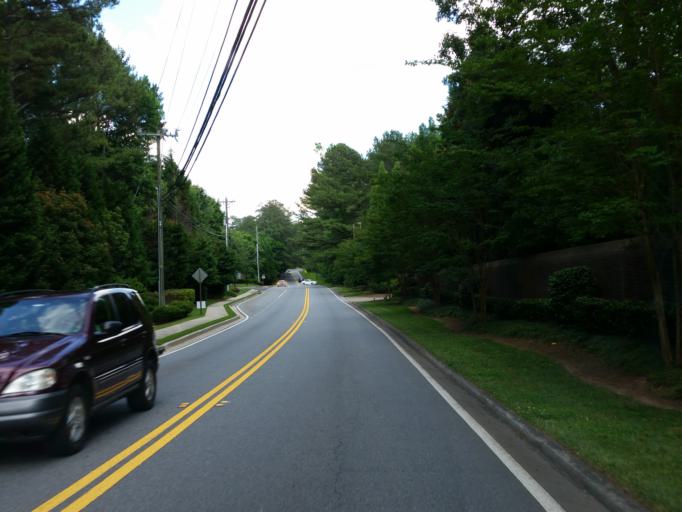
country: US
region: Georgia
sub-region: Fulton County
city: Roswell
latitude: 34.0260
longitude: -84.4118
